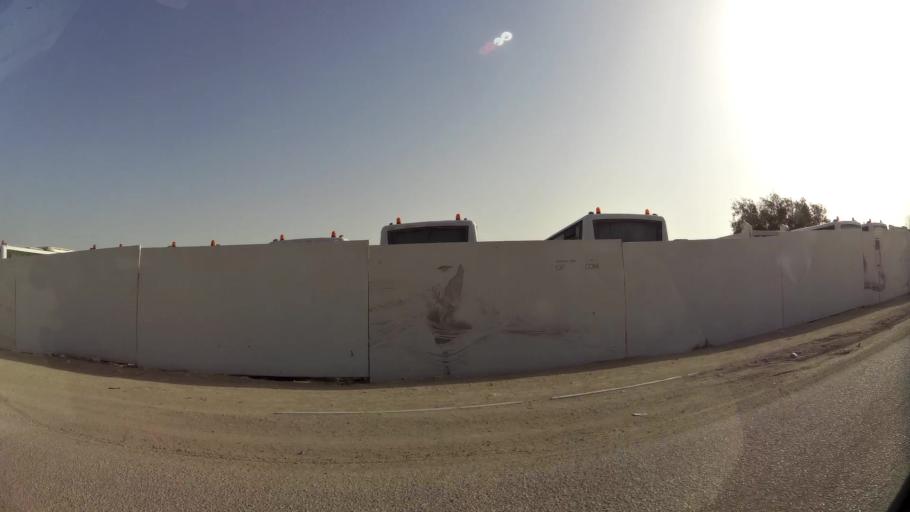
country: QA
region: Baladiyat ar Rayyan
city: Ar Rayyan
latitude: 25.3286
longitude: 51.4296
